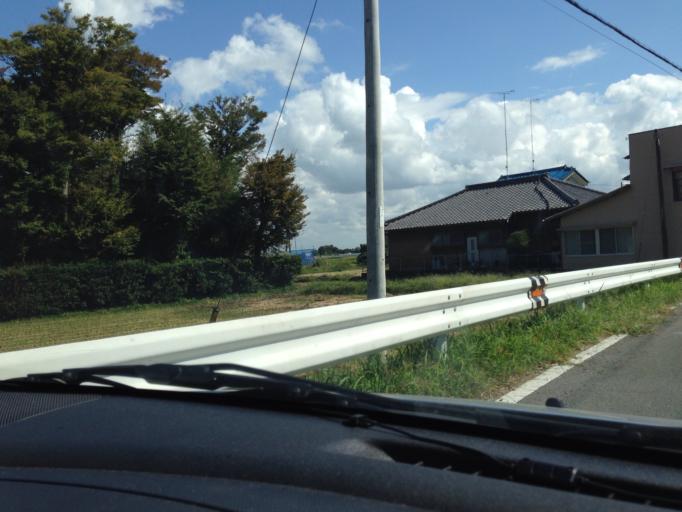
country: JP
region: Ibaraki
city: Inashiki
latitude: 36.0102
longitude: 140.3634
